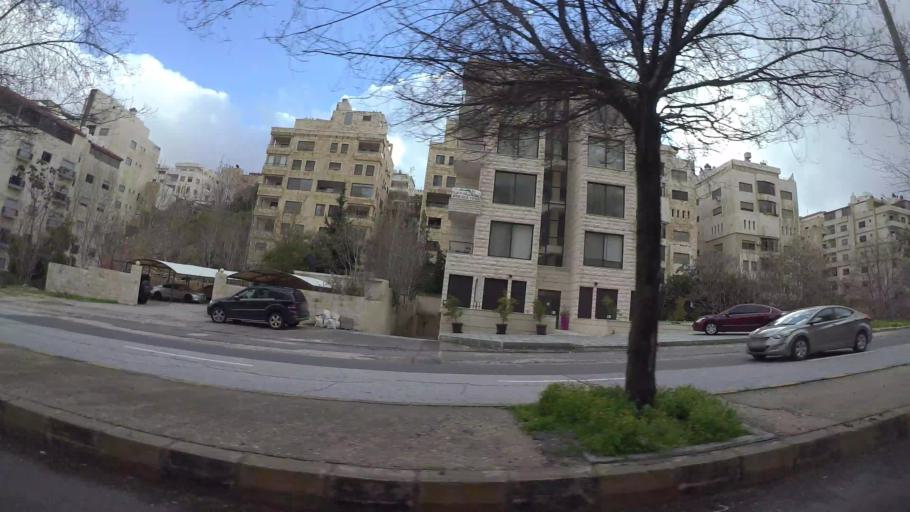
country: JO
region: Amman
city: Al Bunayyat ash Shamaliyah
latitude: 31.9428
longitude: 35.8938
